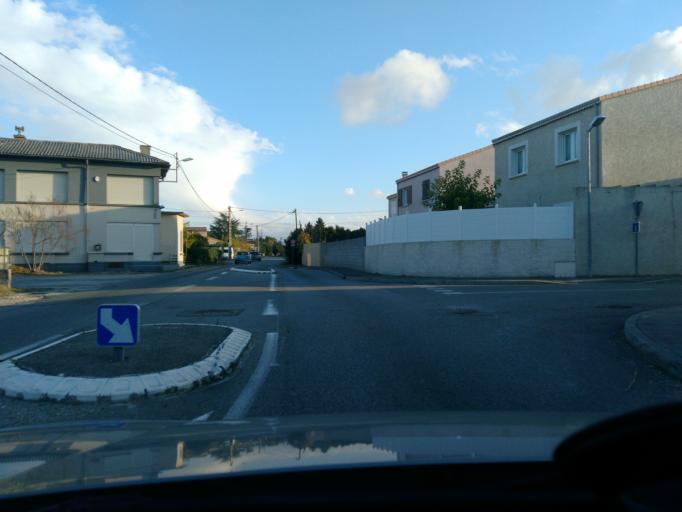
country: FR
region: Rhone-Alpes
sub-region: Departement de la Drome
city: Montelimar
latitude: 44.5351
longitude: 4.7395
